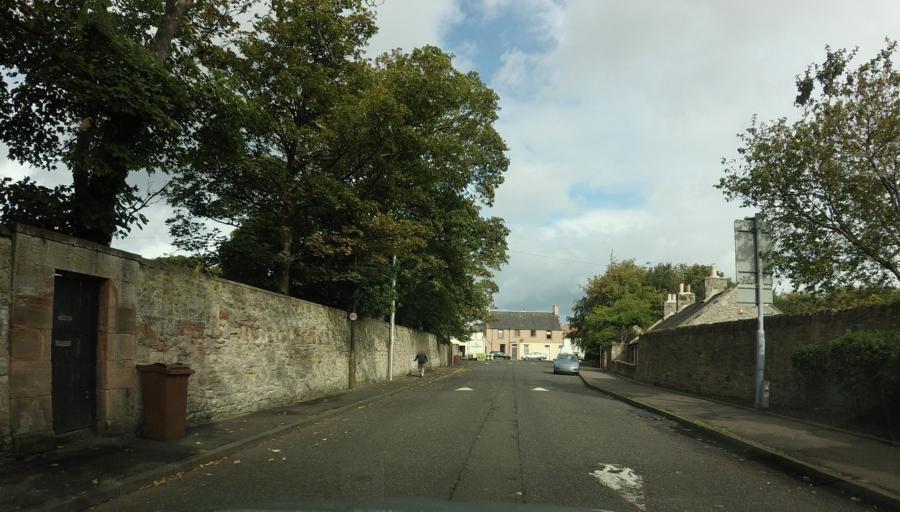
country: GB
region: Scotland
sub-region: East Lothian
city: Prestonpans
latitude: 55.9597
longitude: -2.9793
